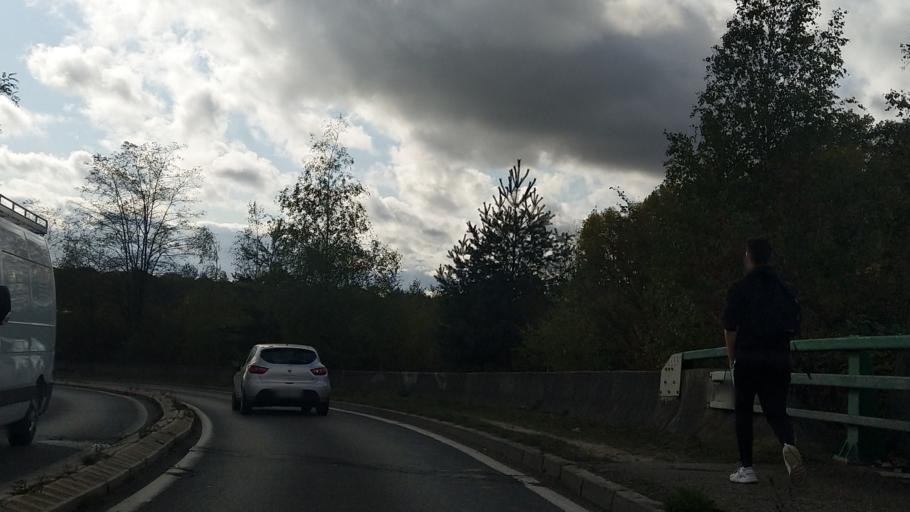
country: FR
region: Ile-de-France
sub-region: Departement du Val-d'Oise
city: Mours
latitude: 49.1281
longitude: 2.2532
